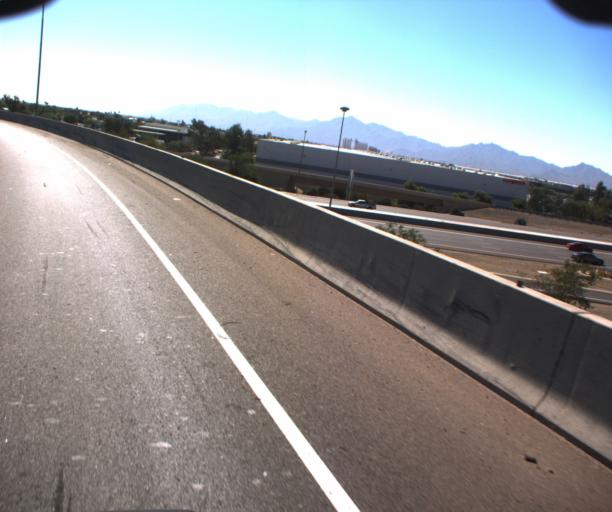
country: US
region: Arizona
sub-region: Maricopa County
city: Tolleson
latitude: 33.4627
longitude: -112.2686
